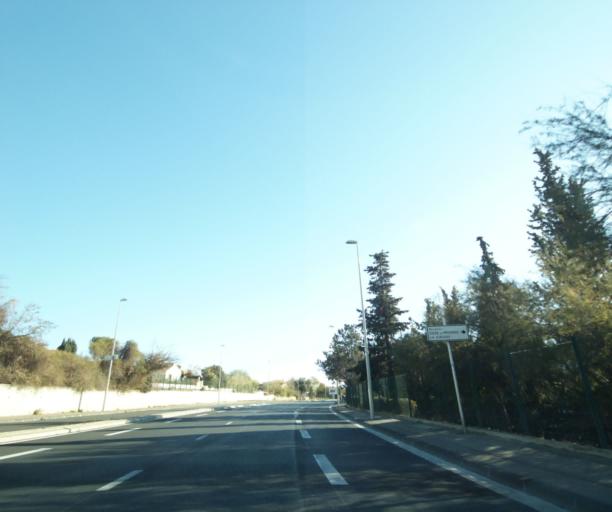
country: FR
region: Provence-Alpes-Cote d'Azur
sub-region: Departement des Bouches-du-Rhone
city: Marseille 14
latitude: 43.3431
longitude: 5.3858
